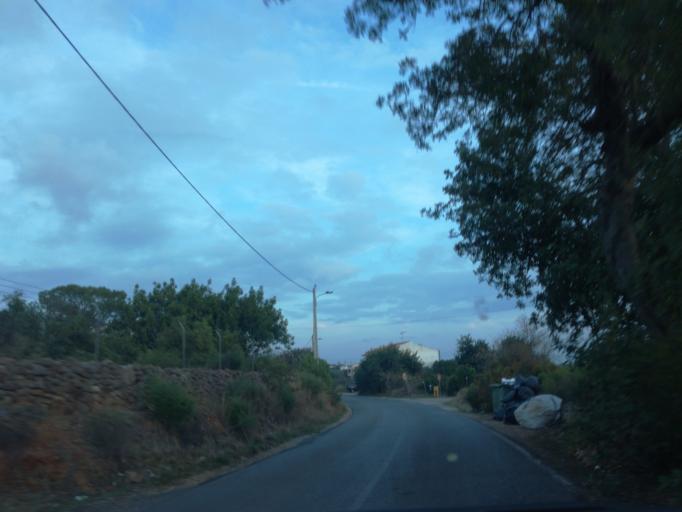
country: PT
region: Faro
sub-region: Sao Bras de Alportel
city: Sao Bras de Alportel
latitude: 37.0886
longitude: -7.8869
